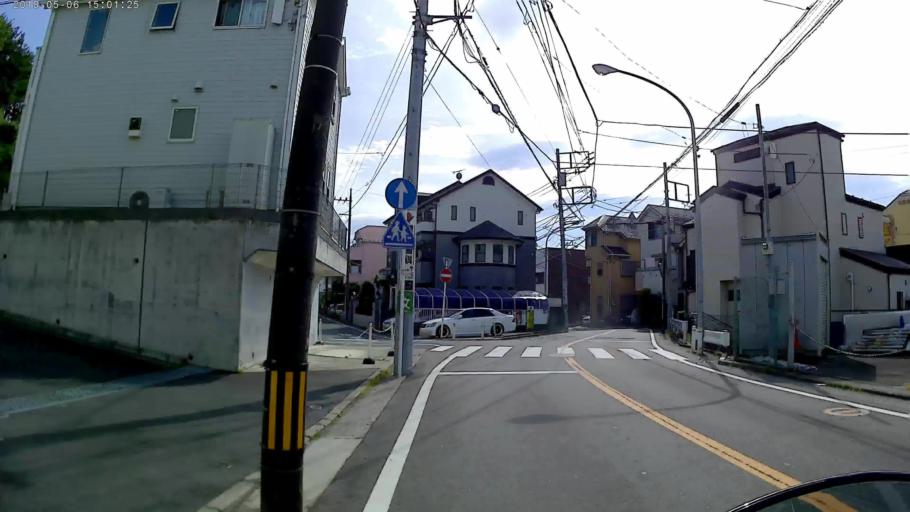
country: JP
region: Kanagawa
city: Yokohama
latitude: 35.4177
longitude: 139.6123
